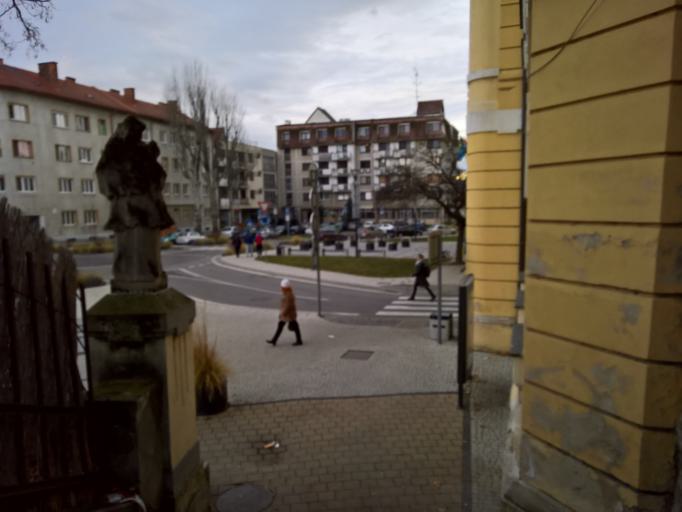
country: SK
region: Nitriansky
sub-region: Okres Nitra
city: Nitra
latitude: 48.3156
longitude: 18.0860
